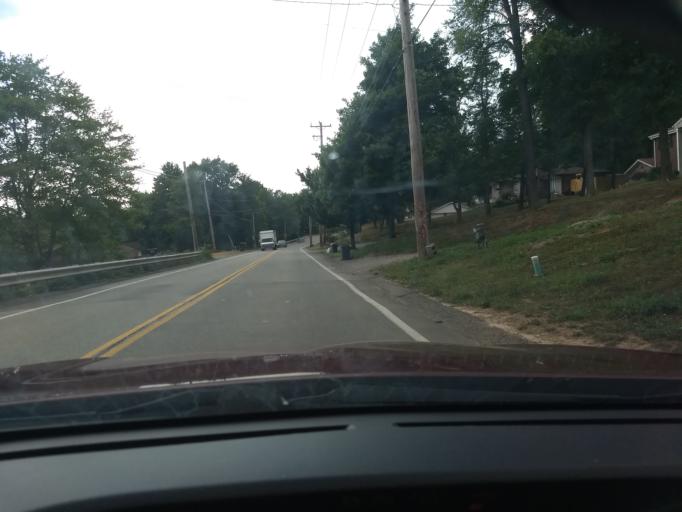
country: US
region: Pennsylvania
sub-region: Allegheny County
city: Curtisville
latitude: 40.6268
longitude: -79.8617
